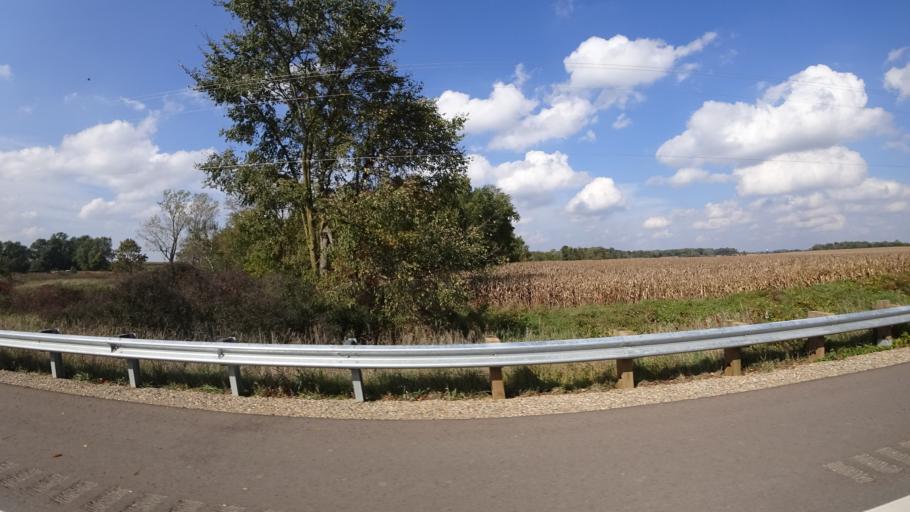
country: US
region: Michigan
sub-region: Calhoun County
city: Athens
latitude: 42.0617
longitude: -85.2552
